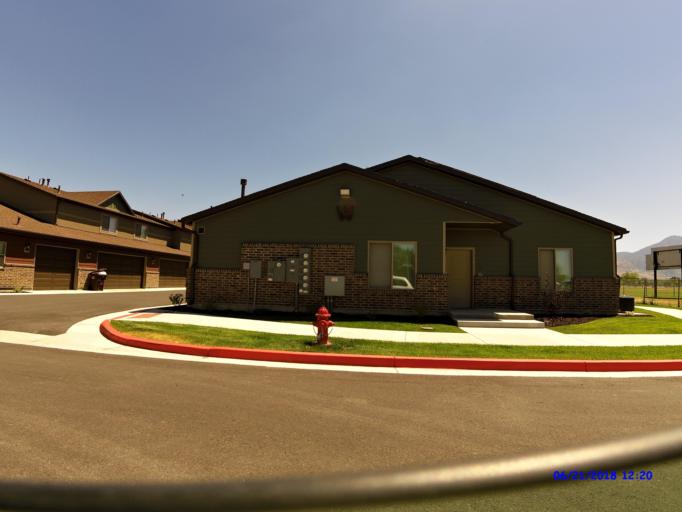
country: US
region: Utah
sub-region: Weber County
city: Harrisville
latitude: 41.2820
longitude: -111.9996
